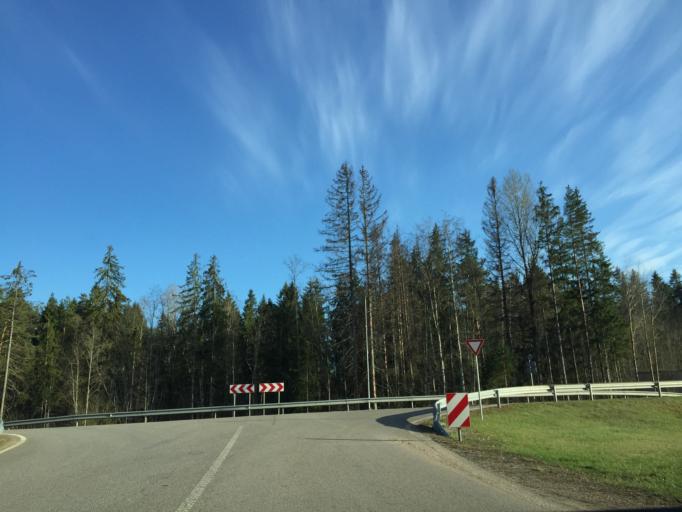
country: LV
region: Valkas Rajons
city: Valka
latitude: 57.7863
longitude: 25.9962
